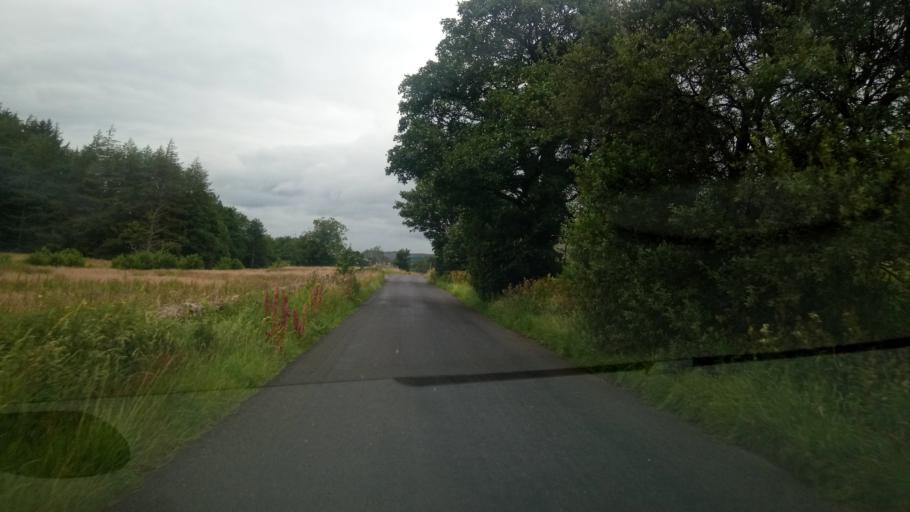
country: GB
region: England
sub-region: Cumbria
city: Kirkby Stephen
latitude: 54.3899
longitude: -2.3370
